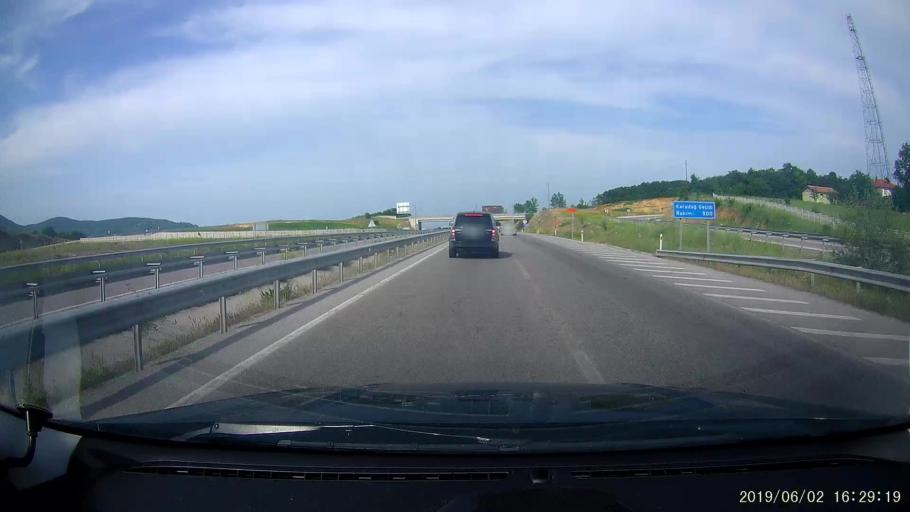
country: TR
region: Samsun
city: Ladik
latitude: 41.0126
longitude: 35.8670
